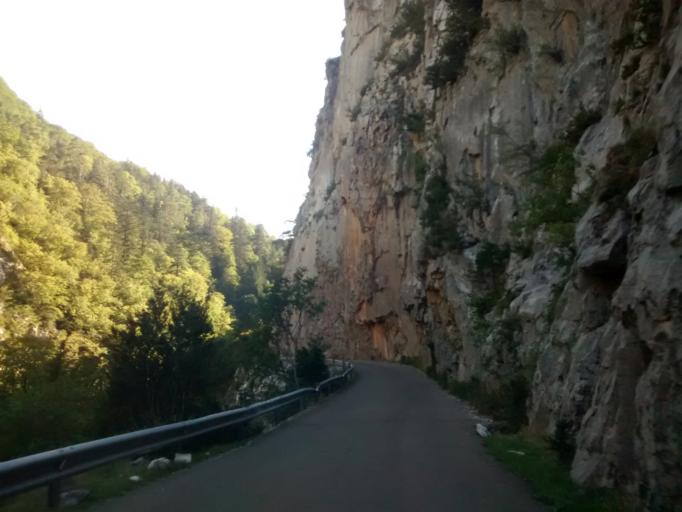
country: ES
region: Aragon
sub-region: Provincia de Huesca
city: Aragues del Puerto
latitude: 42.8055
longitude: -0.7152
